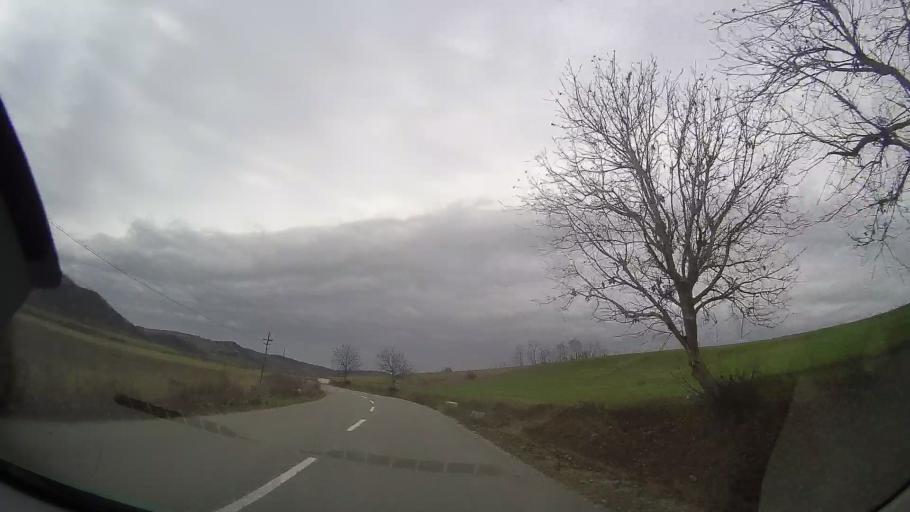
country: RO
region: Bistrita-Nasaud
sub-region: Comuna Milas
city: Milas
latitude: 46.7967
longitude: 24.4216
